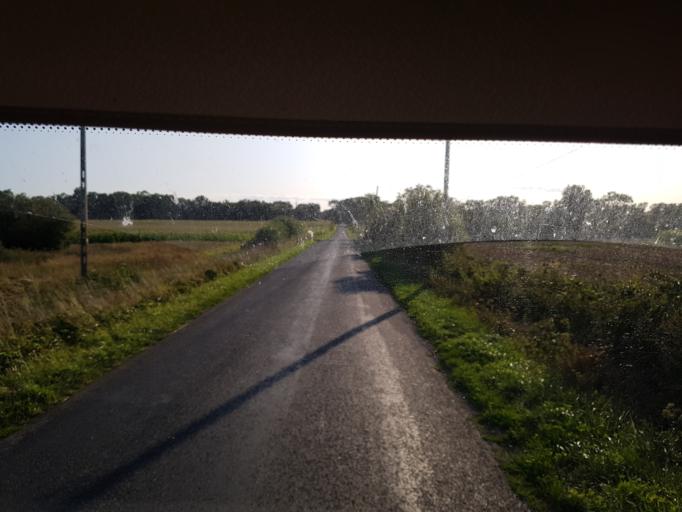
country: FR
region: Rhone-Alpes
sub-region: Departement de l'Ain
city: Villars-les-Dombes
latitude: 45.9673
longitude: 5.0738
